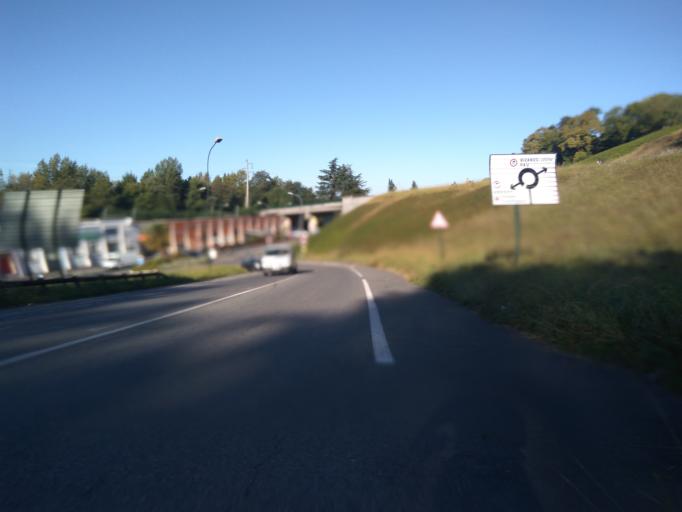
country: FR
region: Aquitaine
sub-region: Departement des Pyrenees-Atlantiques
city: Bizanos
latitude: 43.2844
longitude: -0.3448
